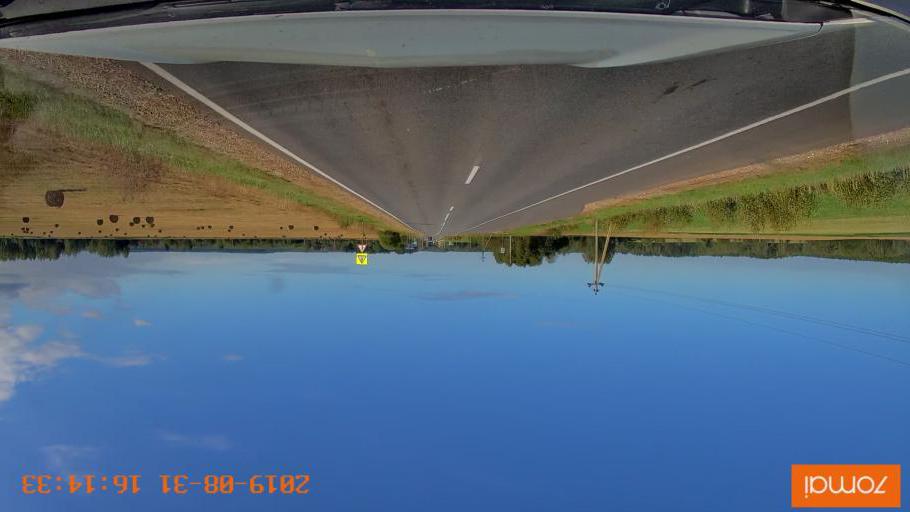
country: RU
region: Kaluga
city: Nikola-Lenivets
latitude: 54.5662
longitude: 35.4695
